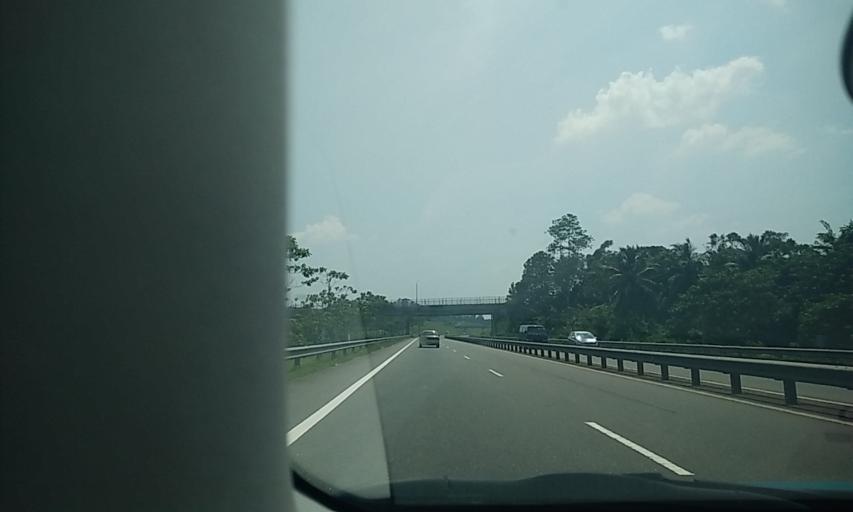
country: LK
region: Western
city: Horana South
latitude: 6.7544
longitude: 79.9936
